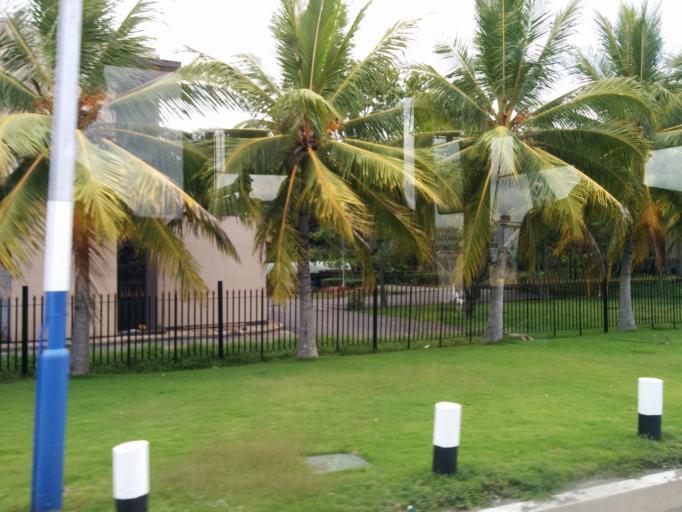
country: LK
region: Western
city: Katunayaka
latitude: 7.1785
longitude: 79.8865
